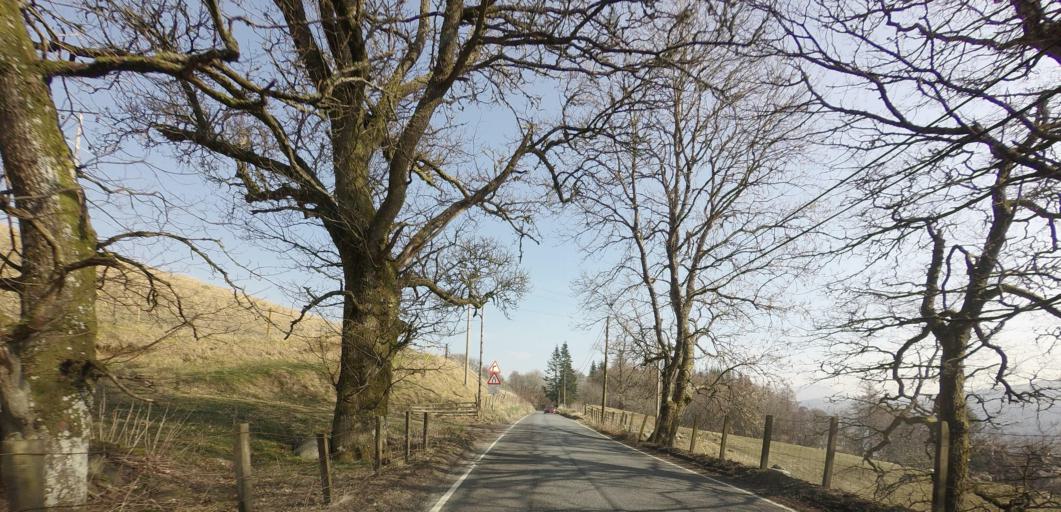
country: GB
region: Scotland
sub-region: Stirling
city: Callander
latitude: 56.4984
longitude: -4.2474
